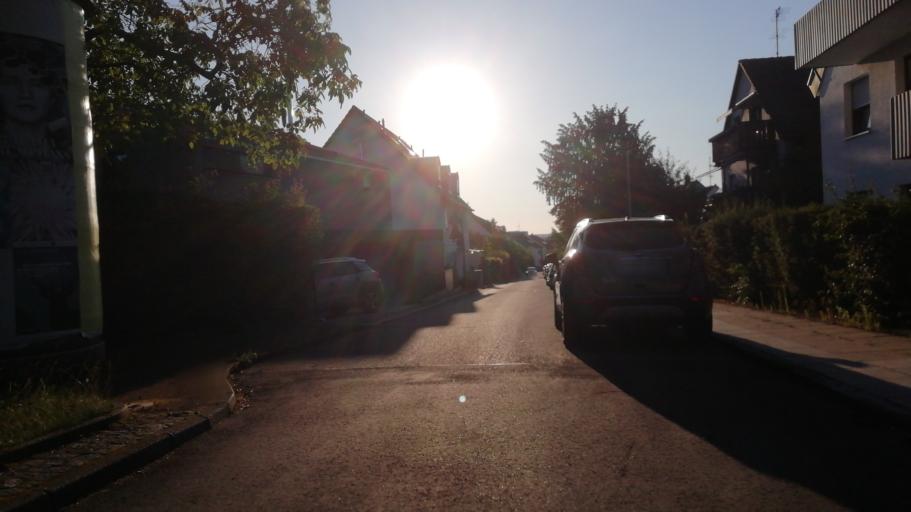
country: DE
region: Baden-Wuerttemberg
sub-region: Regierungsbezirk Stuttgart
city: Korntal
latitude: 48.8183
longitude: 9.1118
